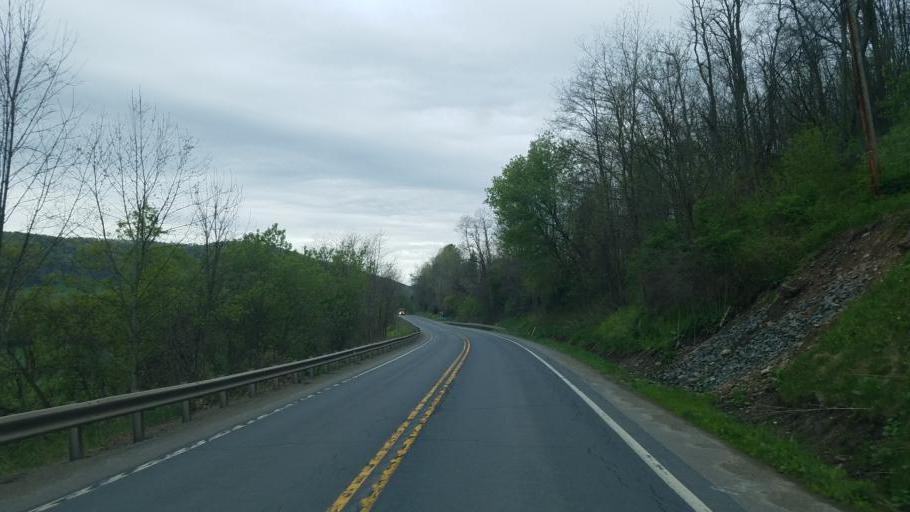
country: US
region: Pennsylvania
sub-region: Tioga County
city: Westfield
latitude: 41.9426
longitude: -77.4772
